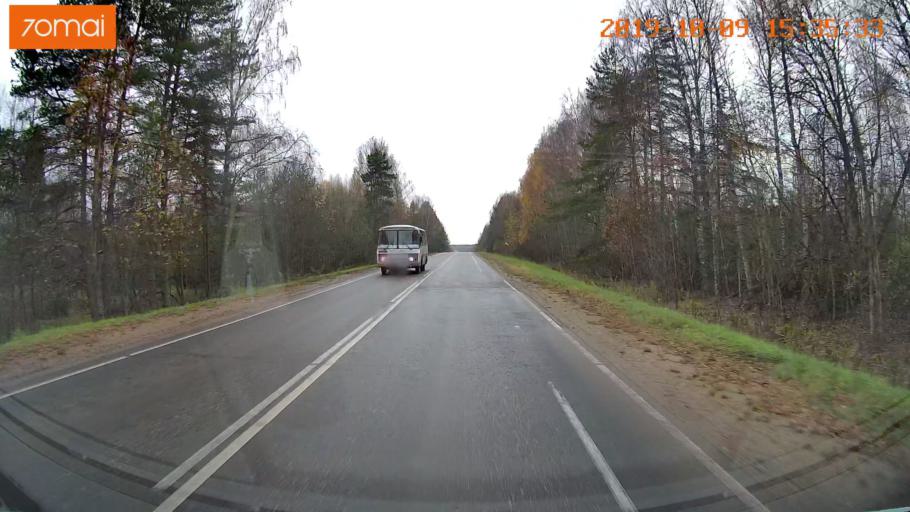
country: RU
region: Kostroma
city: Oktyabr'skiy
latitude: 57.9310
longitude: 41.2249
